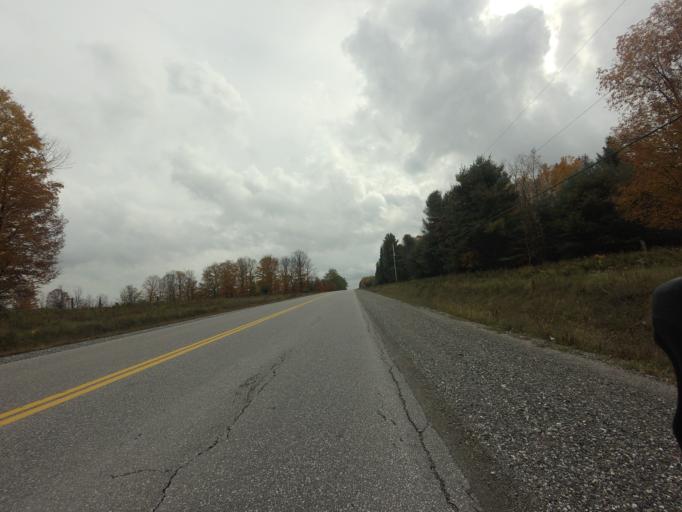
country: CA
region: Ontario
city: Perth
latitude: 45.0993
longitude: -76.4675
